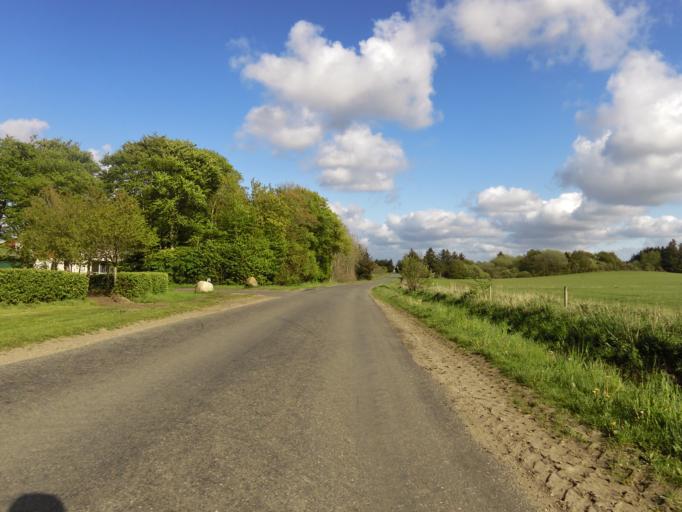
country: DK
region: South Denmark
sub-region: Esbjerg Kommune
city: Ribe
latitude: 55.2634
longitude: 8.7562
